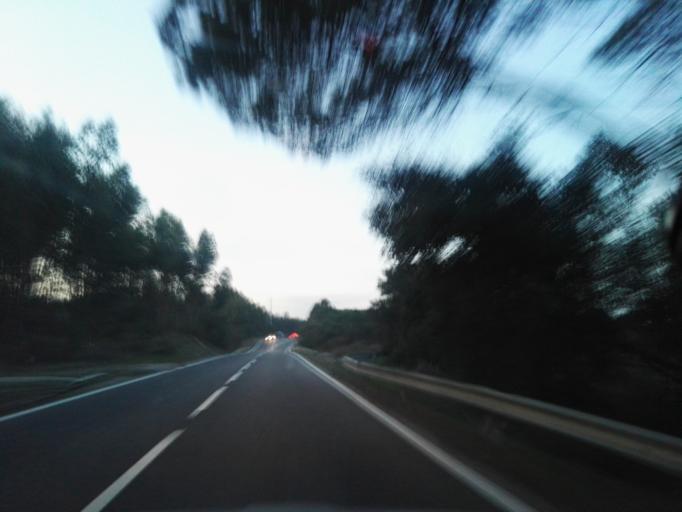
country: PT
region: Santarem
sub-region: Benavente
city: Benavente
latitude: 38.9347
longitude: -8.7820
